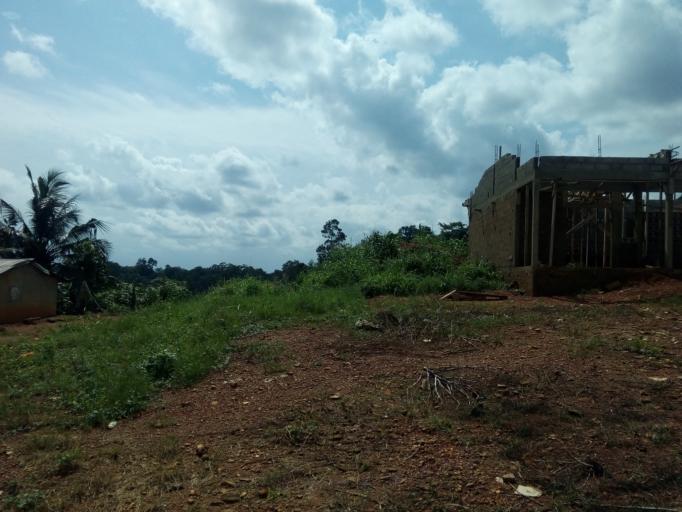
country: CI
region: Sud-Comoe
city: Mafere
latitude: 5.2949
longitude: -2.7862
